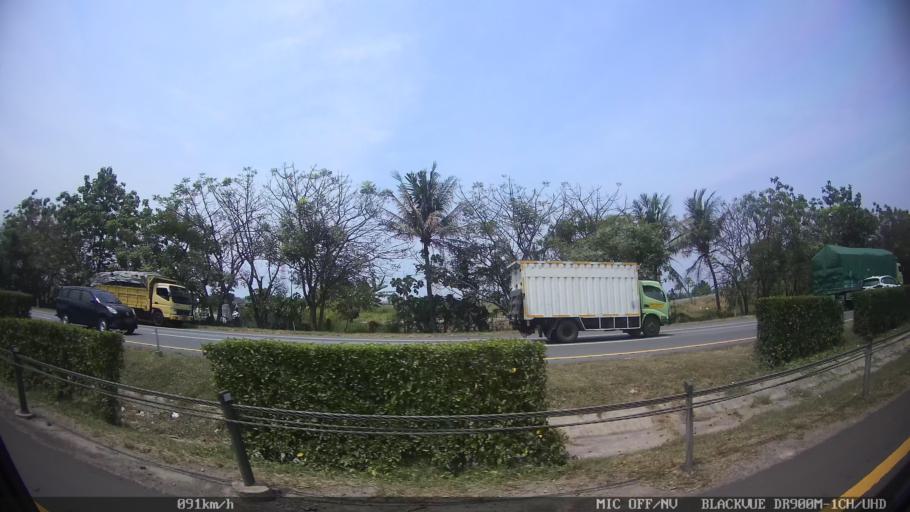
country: ID
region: Banten
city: Bojonegara
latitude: -6.0321
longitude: 106.1000
